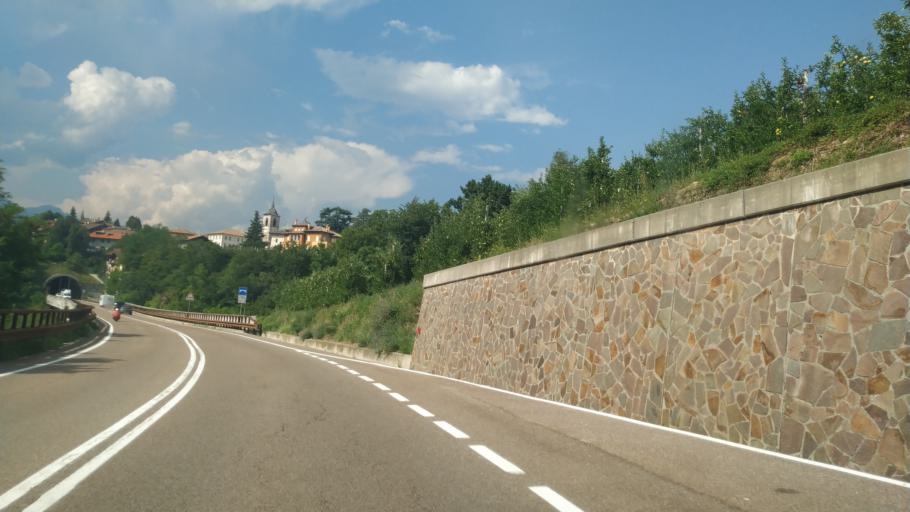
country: IT
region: Trentino-Alto Adige
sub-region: Provincia di Trento
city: Taio
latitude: 46.3167
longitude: 11.0674
